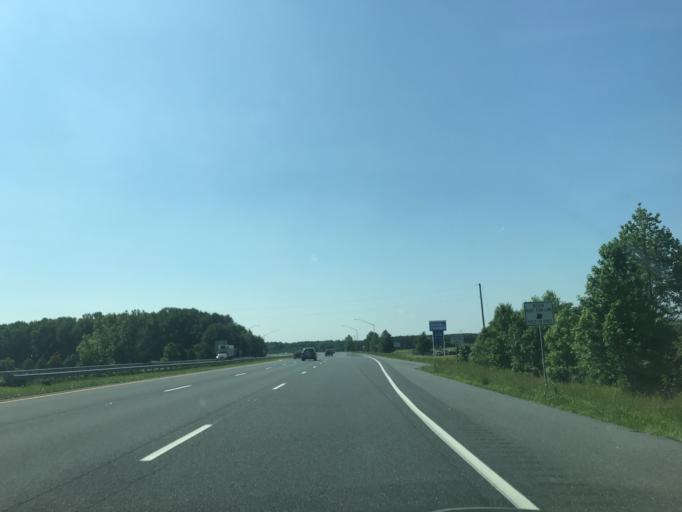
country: US
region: Maryland
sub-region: Wicomico County
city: Hebron
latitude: 38.4084
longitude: -75.6409
